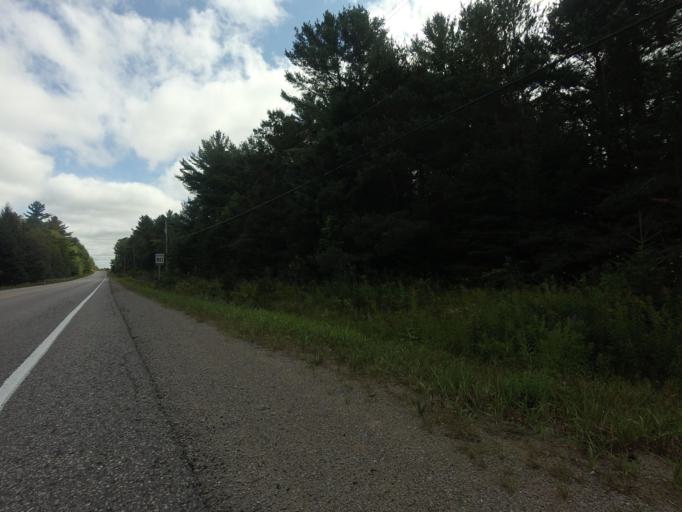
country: CA
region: Ontario
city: Omemee
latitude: 44.8037
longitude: -78.6135
